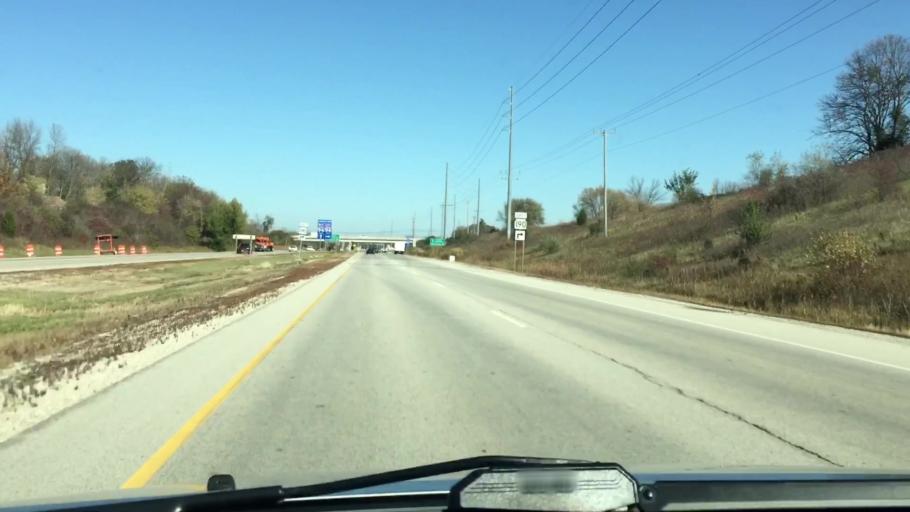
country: US
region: Wisconsin
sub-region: Waukesha County
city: Pewaukee
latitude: 43.0787
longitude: -88.2056
